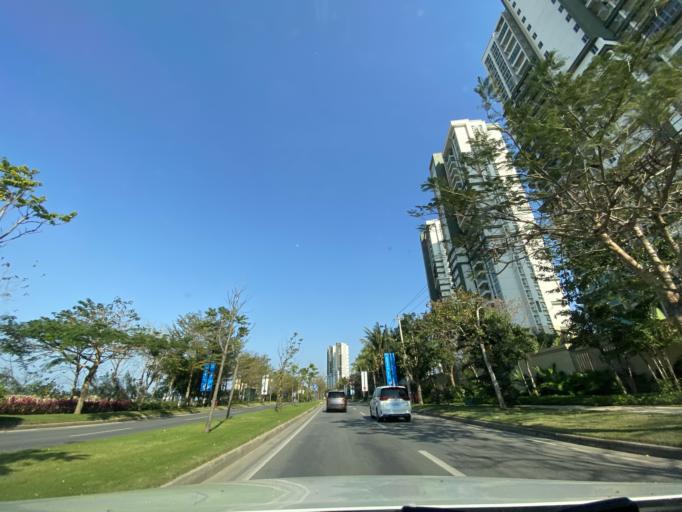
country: CN
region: Hainan
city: Xincun
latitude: 18.4207
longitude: 109.9180
